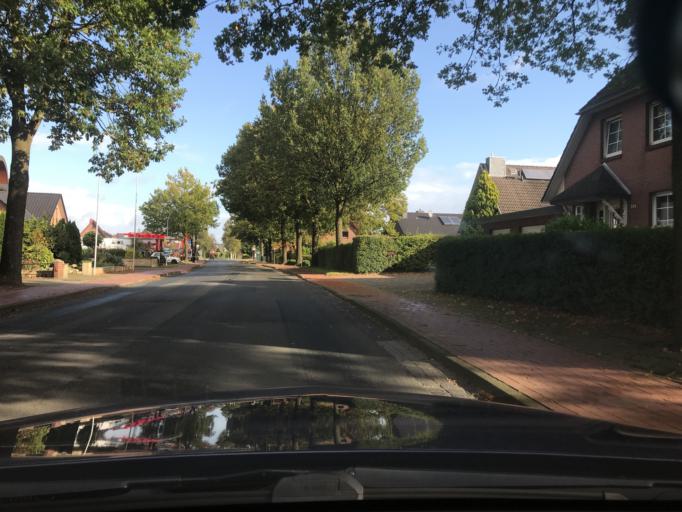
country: DE
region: Lower Saxony
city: Ahlerstedt
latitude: 53.4080
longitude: 9.4551
